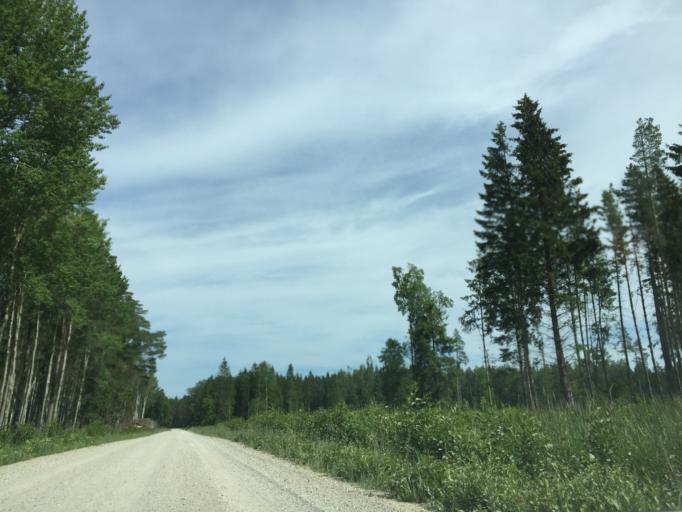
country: LV
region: Dundaga
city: Dundaga
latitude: 57.6207
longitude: 22.5512
